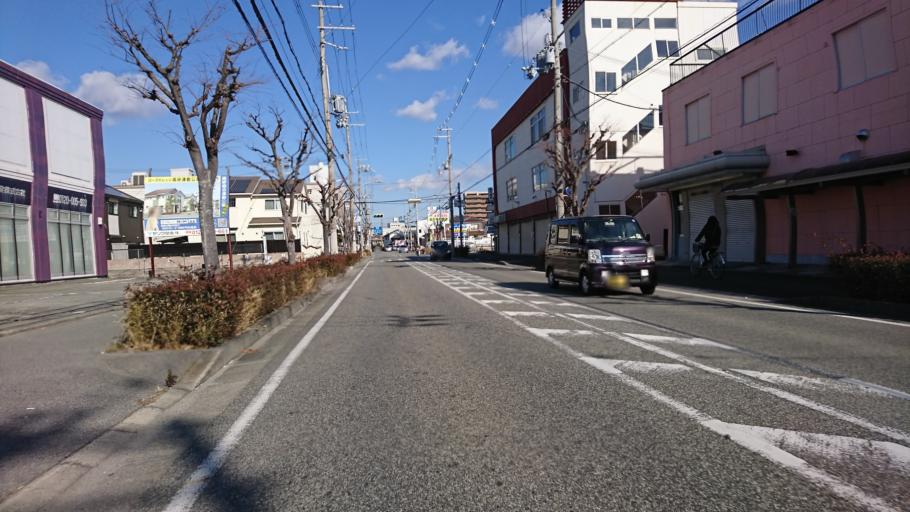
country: JP
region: Hyogo
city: Kakogawacho-honmachi
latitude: 34.7822
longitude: 134.8101
